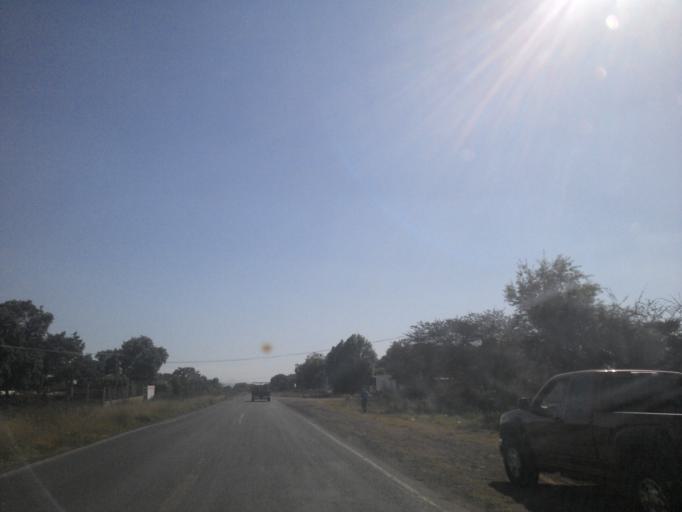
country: MX
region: Jalisco
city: Arandas
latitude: 20.7519
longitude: -102.3046
